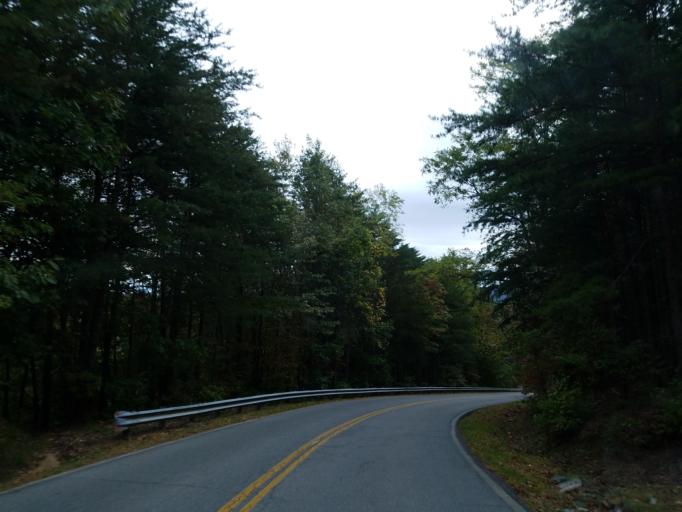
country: US
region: Georgia
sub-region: Dawson County
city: Dawsonville
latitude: 34.5631
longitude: -84.2535
